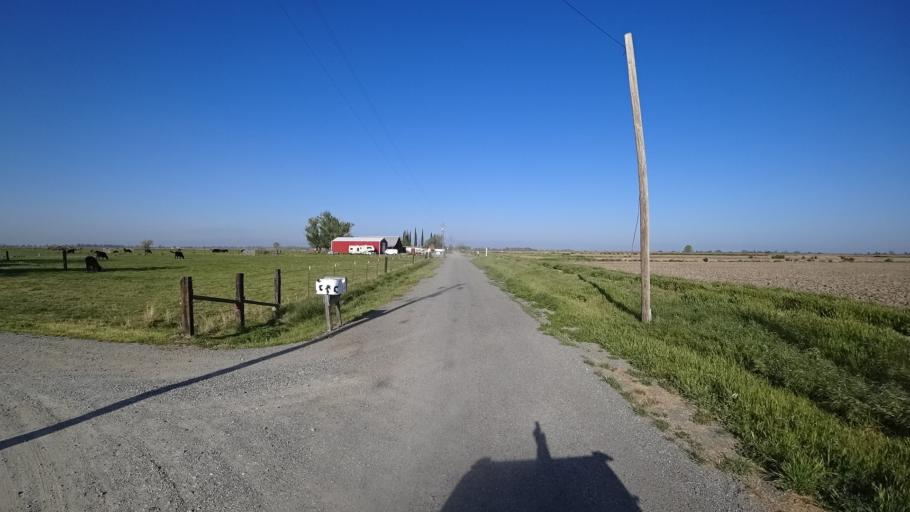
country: US
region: California
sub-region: Glenn County
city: Willows
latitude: 39.5425
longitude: -122.1406
